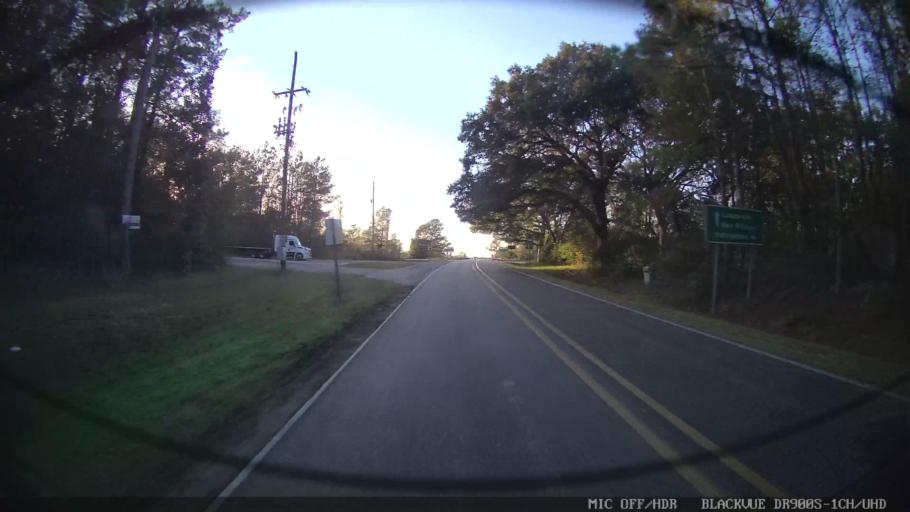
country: US
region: Mississippi
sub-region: Lamar County
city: Lumberton
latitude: 31.0005
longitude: -89.4170
